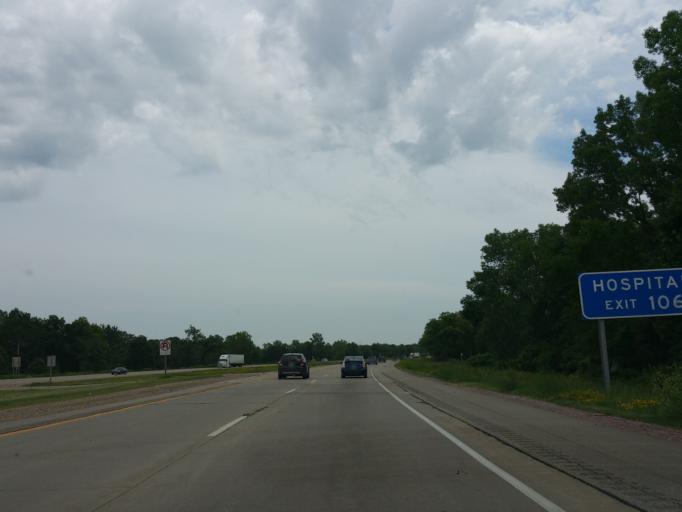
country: US
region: Wisconsin
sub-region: Columbia County
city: Portage
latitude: 43.5197
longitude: -89.5308
